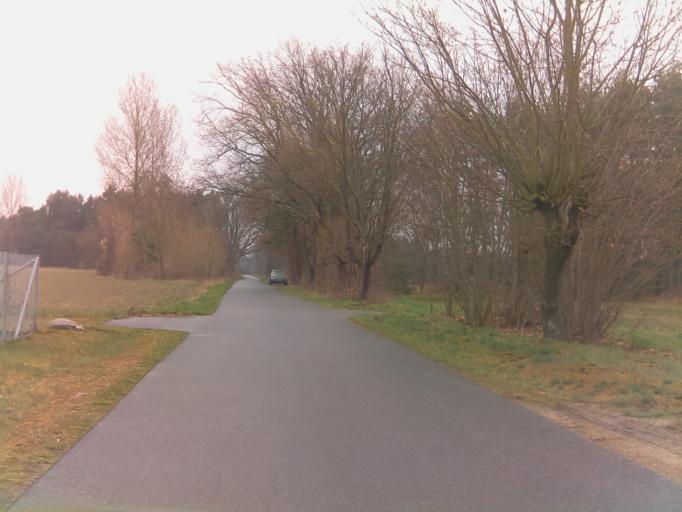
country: DE
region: Brandenburg
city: Lubbenau
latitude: 51.9436
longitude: 13.9909
